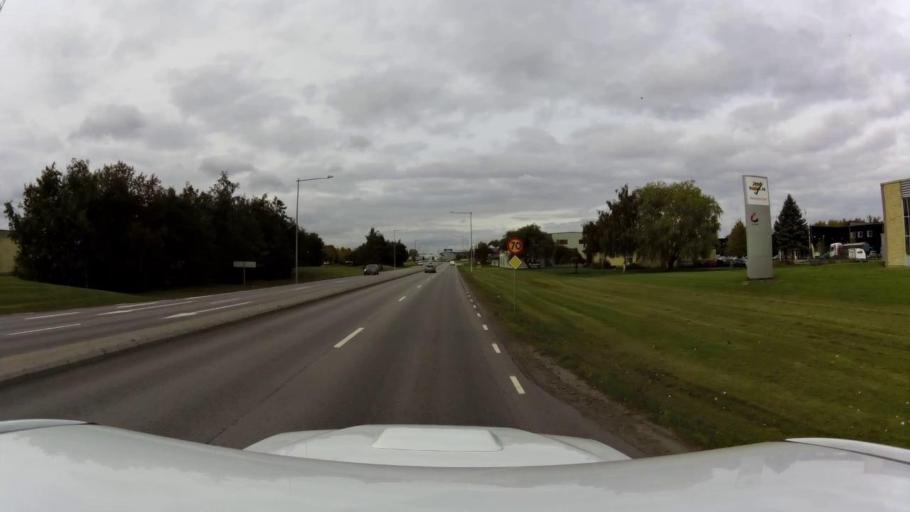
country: SE
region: OEstergoetland
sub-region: Linkopings Kommun
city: Linkoping
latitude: 58.4286
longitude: 15.6070
